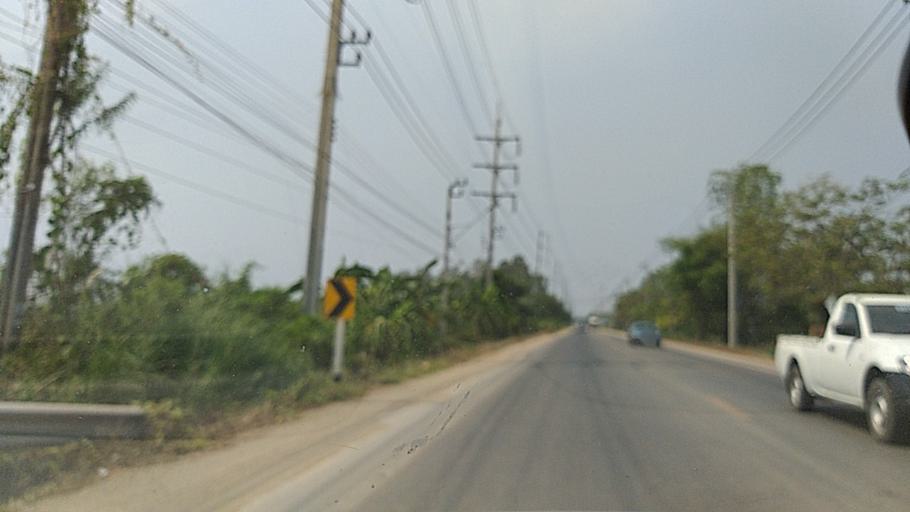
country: TH
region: Nonthaburi
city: Sai Noi
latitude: 13.9338
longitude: 100.3172
